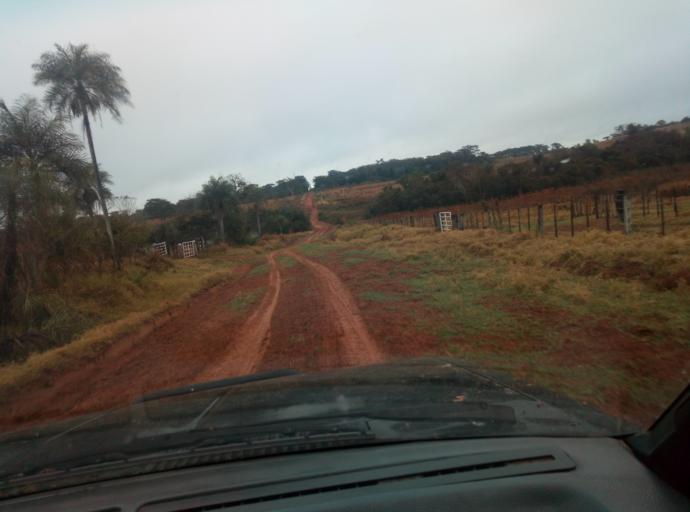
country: PY
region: Caaguazu
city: Carayao
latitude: -25.1929
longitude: -56.3338
